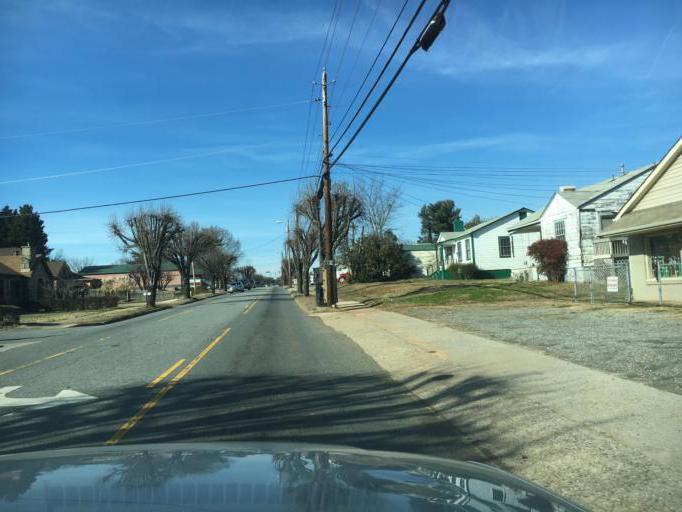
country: US
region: North Carolina
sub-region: Rutherford County
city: Forest City
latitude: 35.3228
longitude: -81.8600
